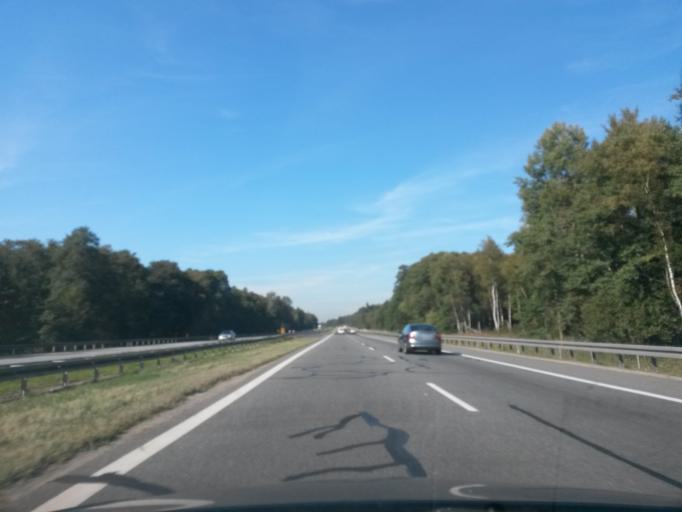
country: PL
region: Lesser Poland Voivodeship
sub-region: Powiat chrzanowski
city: Bolecin
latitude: 50.1269
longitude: 19.4853
